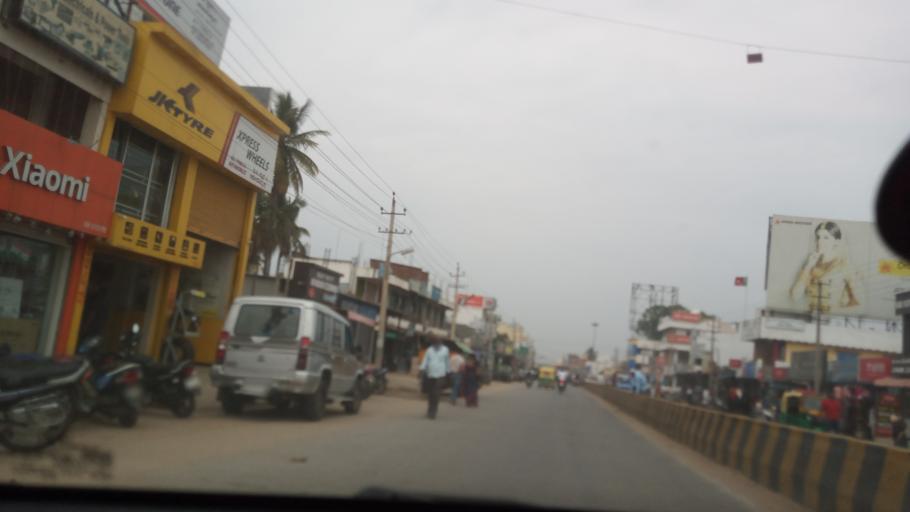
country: IN
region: Karnataka
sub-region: Chamrajnagar
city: Chamrajnagar
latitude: 11.9246
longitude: 76.9399
